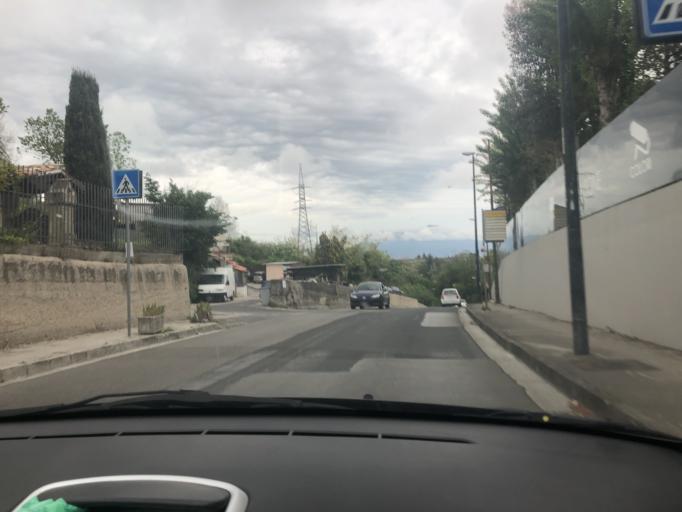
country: IT
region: Campania
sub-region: Provincia di Napoli
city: Torre Caracciolo
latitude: 40.8632
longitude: 14.2105
